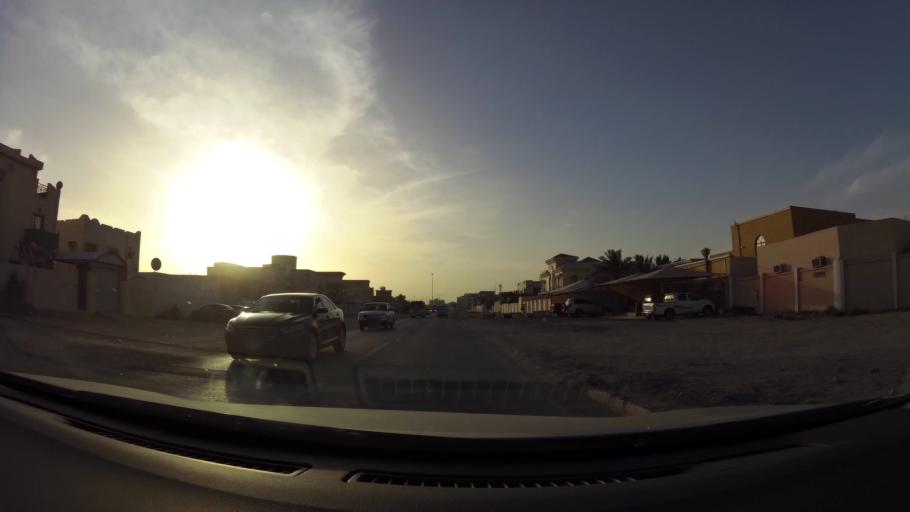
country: QA
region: Al Wakrah
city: Al Wakrah
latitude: 25.1494
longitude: 51.6056
